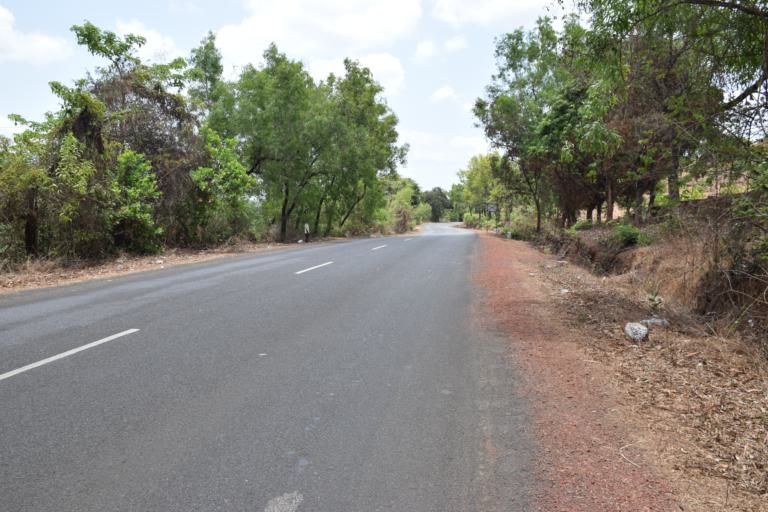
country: IN
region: Maharashtra
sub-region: Ratnagiri
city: Rajapur
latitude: 16.6810
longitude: 73.5411
